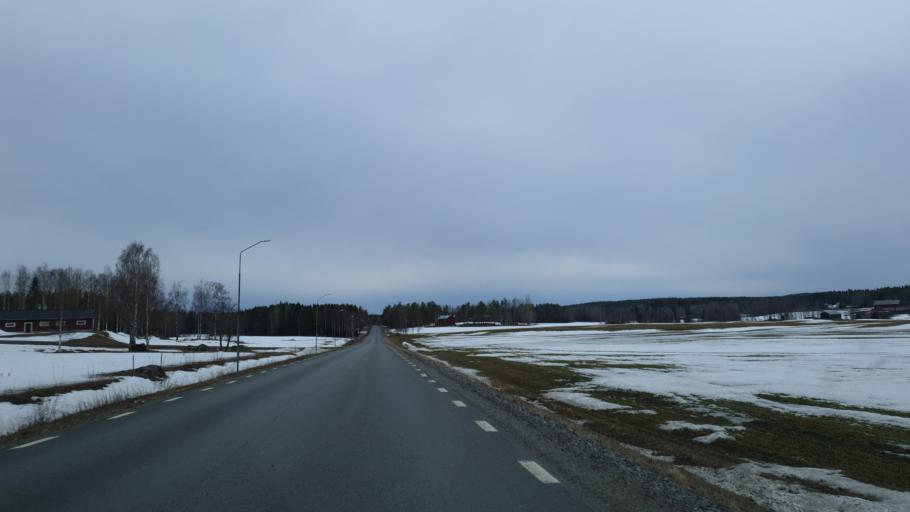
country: SE
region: Vaesterbotten
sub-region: Robertsfors Kommun
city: Robertsfors
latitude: 64.3809
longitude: 20.8985
